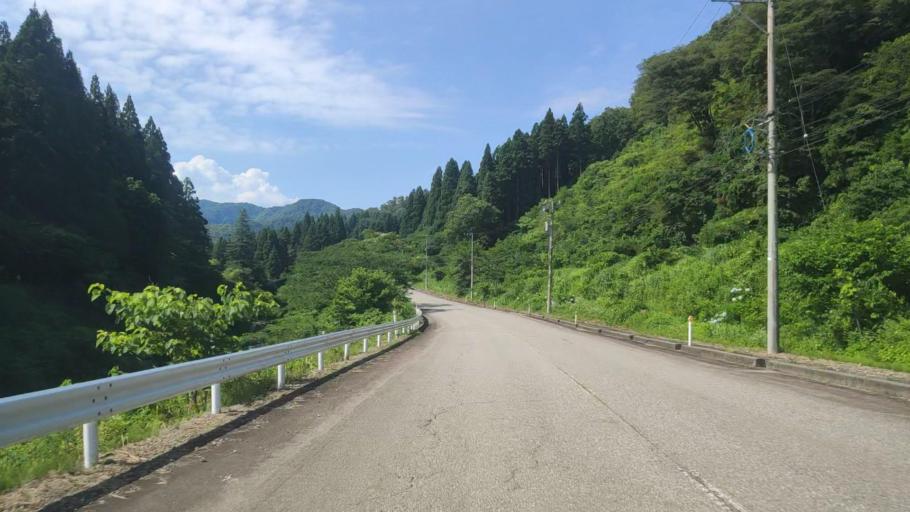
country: JP
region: Ishikawa
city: Komatsu
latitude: 36.3123
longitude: 136.5290
